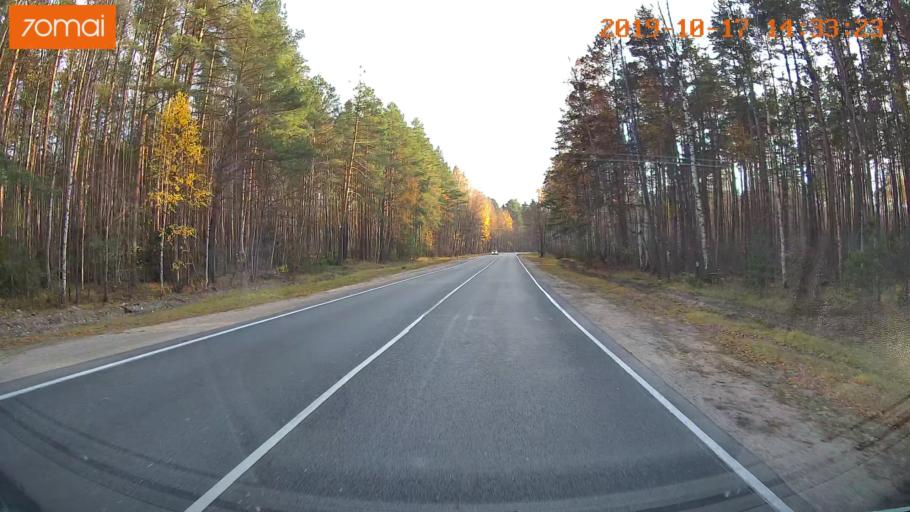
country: RU
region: Rjazan
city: Solotcha
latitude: 54.9240
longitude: 39.9969
